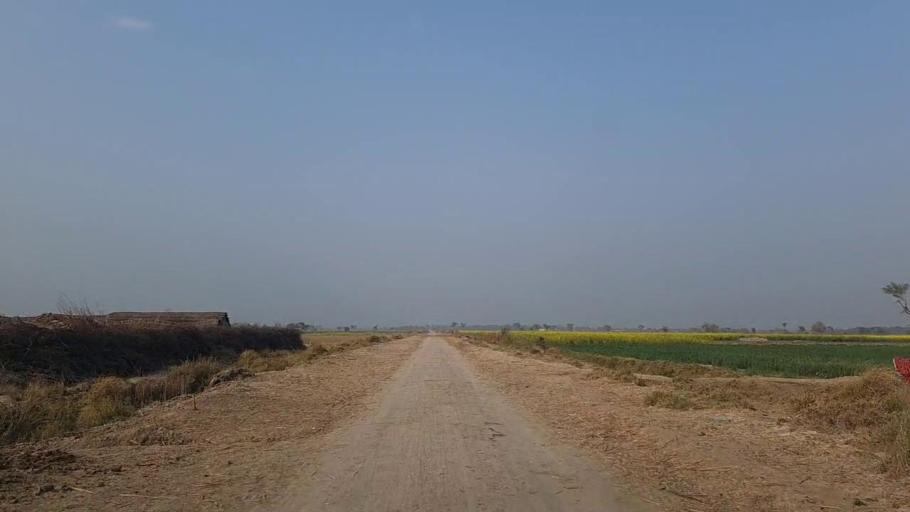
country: PK
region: Sindh
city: Jam Sahib
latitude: 26.3347
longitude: 68.5147
